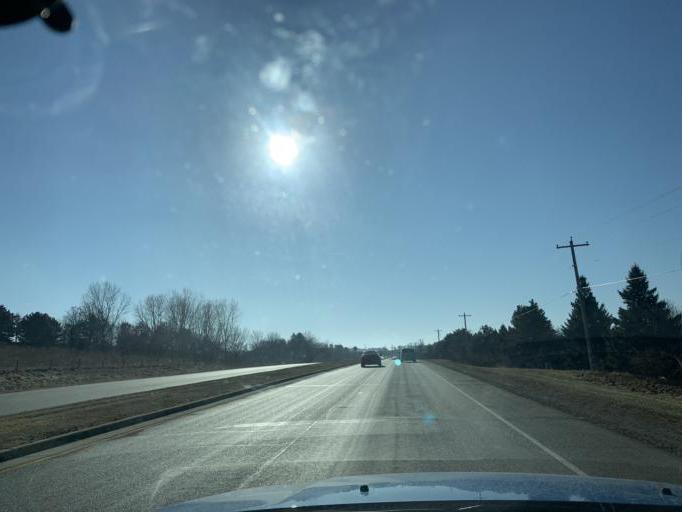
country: US
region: Wisconsin
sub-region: Dane County
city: Verona
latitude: 42.9831
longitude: -89.5140
